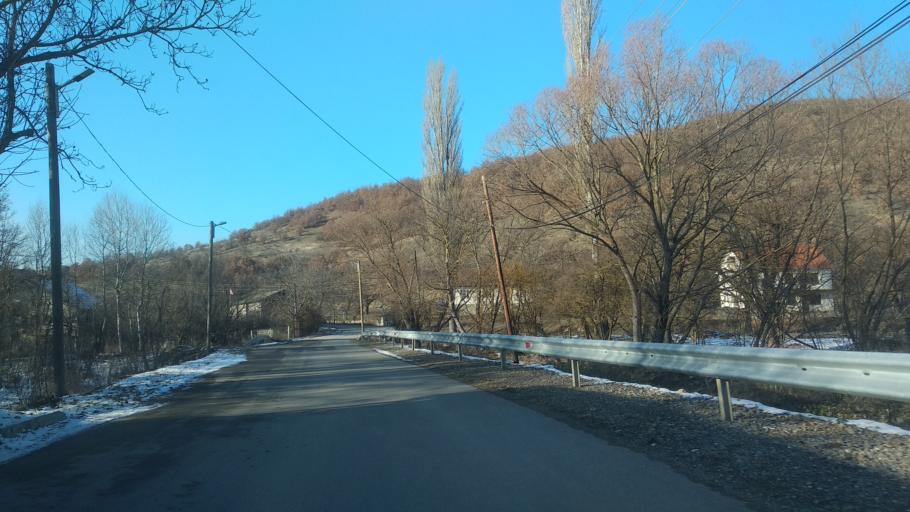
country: XK
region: Pristina
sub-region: Komuna e Prishtines
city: Pristina
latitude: 42.7151
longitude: 21.1690
